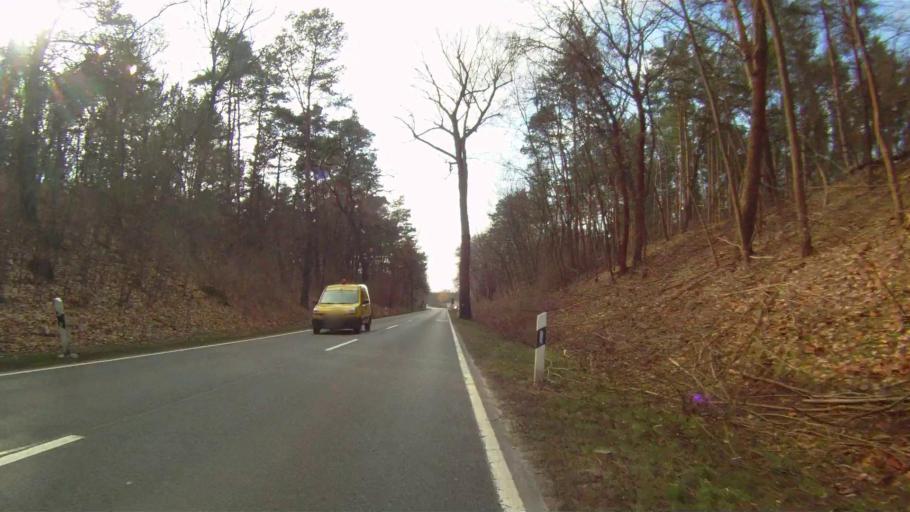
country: DE
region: Berlin
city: Muggelheim
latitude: 52.3756
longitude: 13.7120
